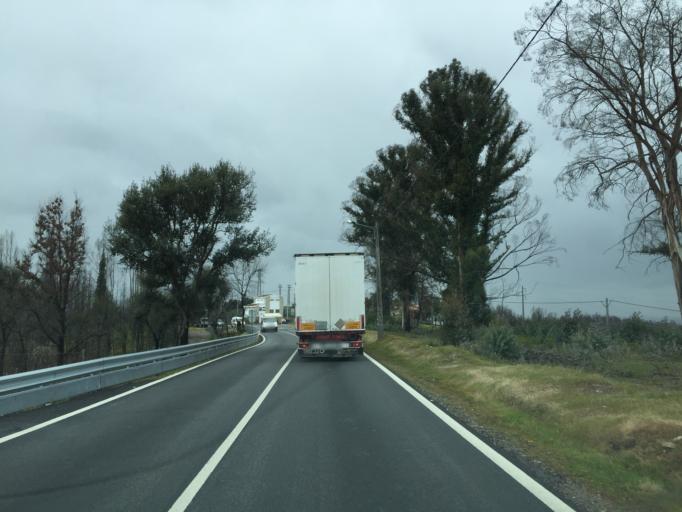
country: PT
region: Coimbra
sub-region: Tabua
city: Tabua
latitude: 40.3288
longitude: -7.9453
